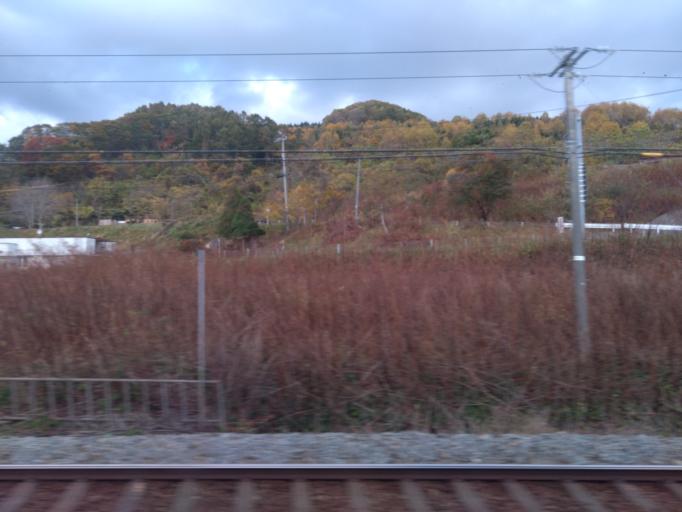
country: JP
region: Hokkaido
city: Niseko Town
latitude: 42.5873
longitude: 140.7075
